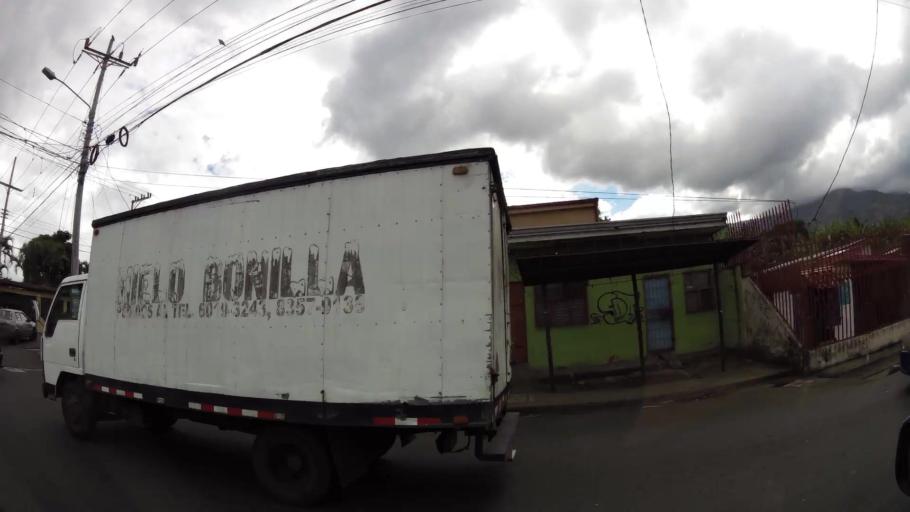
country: CR
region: San Jose
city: Alajuelita
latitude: 9.8967
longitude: -84.0904
